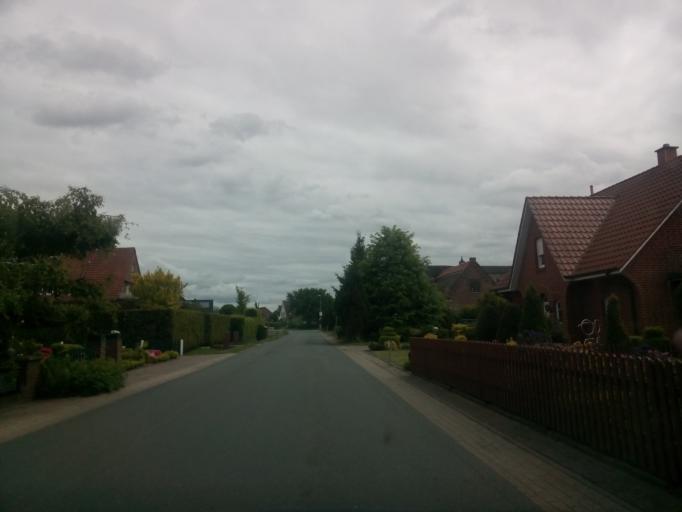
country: DE
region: Lower Saxony
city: Lemwerder
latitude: 53.1760
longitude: 8.5615
